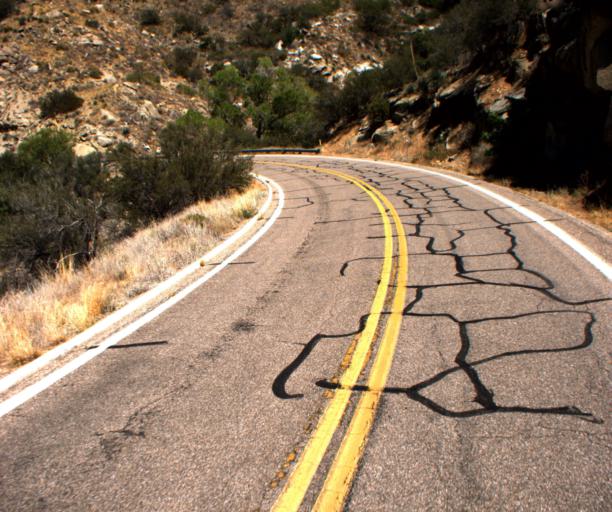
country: US
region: Arizona
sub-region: Pima County
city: Sells
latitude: 31.9743
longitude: -111.6052
